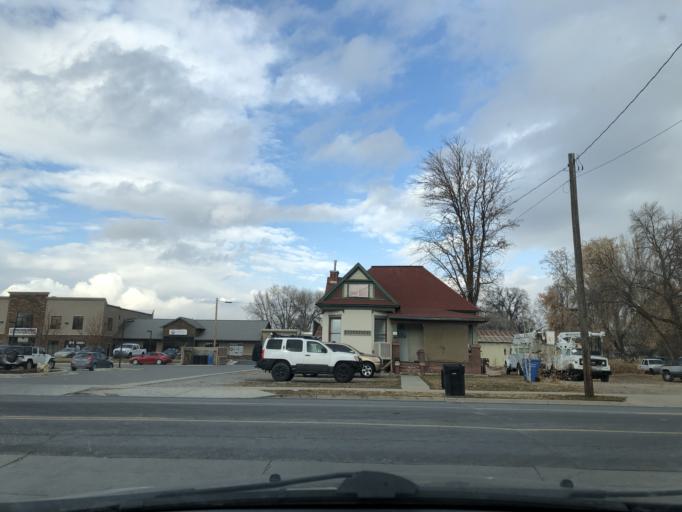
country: US
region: Utah
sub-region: Cache County
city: Logan
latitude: 41.7258
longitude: -111.8341
